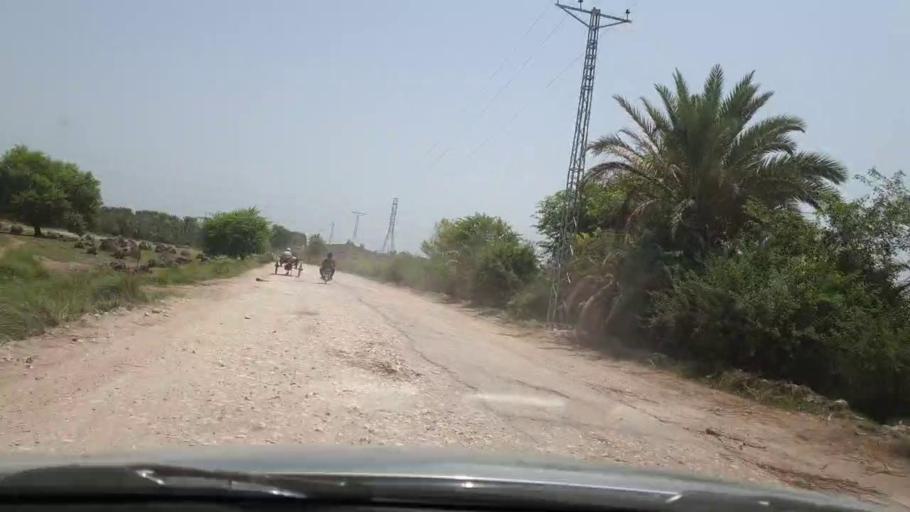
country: PK
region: Sindh
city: Pano Aqil
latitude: 27.8585
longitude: 69.0939
